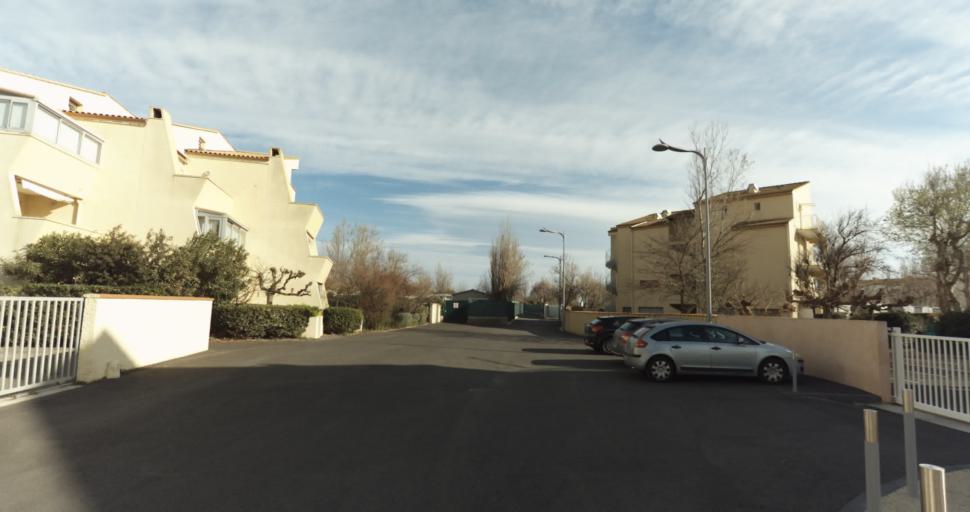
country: FR
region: Languedoc-Roussillon
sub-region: Departement de l'Herault
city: Marseillan
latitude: 43.3128
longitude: 3.5473
